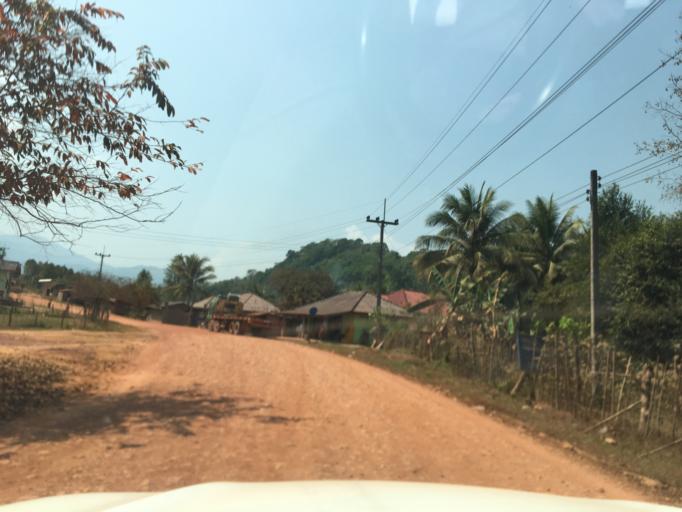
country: LA
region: Bolikhamxai
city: Bolikhan
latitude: 18.7503
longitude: 103.5951
